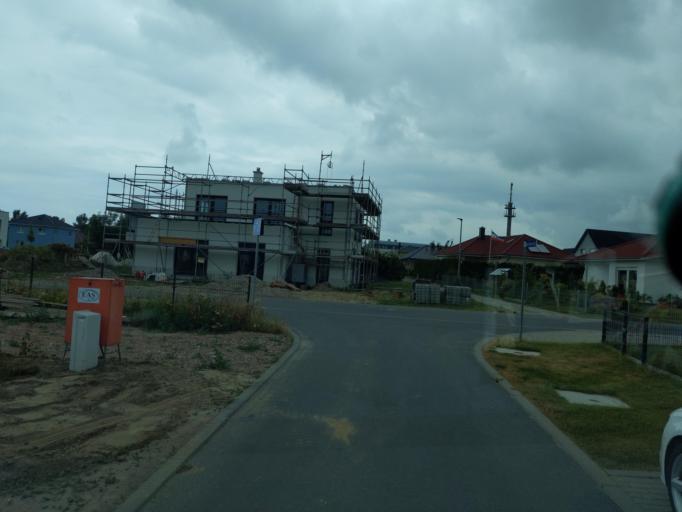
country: DE
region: Mecklenburg-Vorpommern
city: Ribnitz-Damgarten
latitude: 54.2339
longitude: 12.4424
